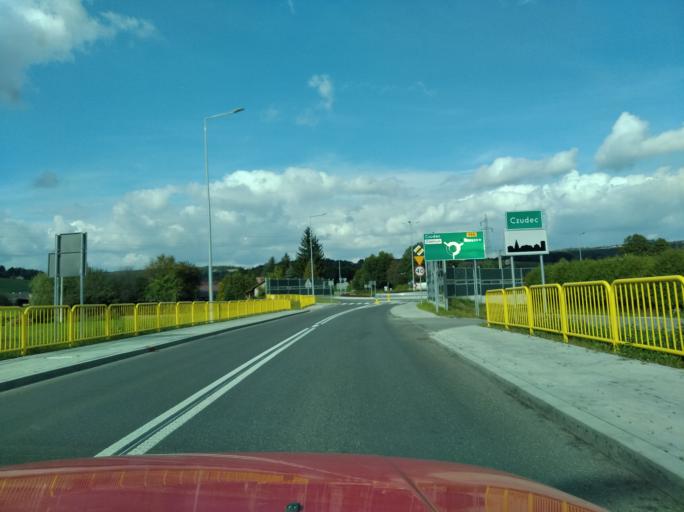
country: PL
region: Subcarpathian Voivodeship
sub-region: Powiat strzyzowski
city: Czudec
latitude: 49.9356
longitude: 21.8164
